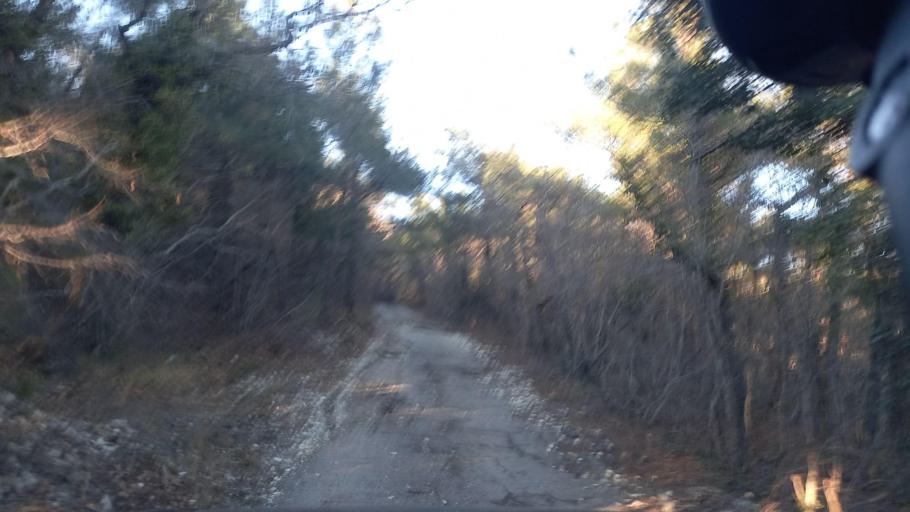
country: RU
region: Krasnodarskiy
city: Kabardinka
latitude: 44.6105
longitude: 37.9408
